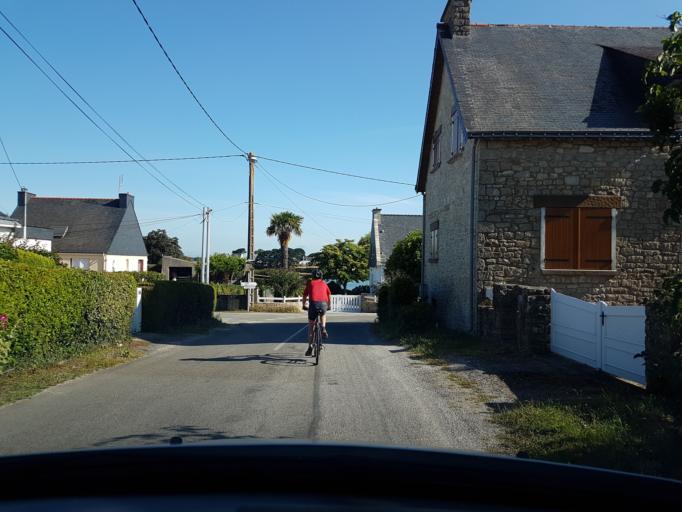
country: FR
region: Brittany
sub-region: Departement du Morbihan
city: Belz
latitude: 47.6764
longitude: -3.1889
